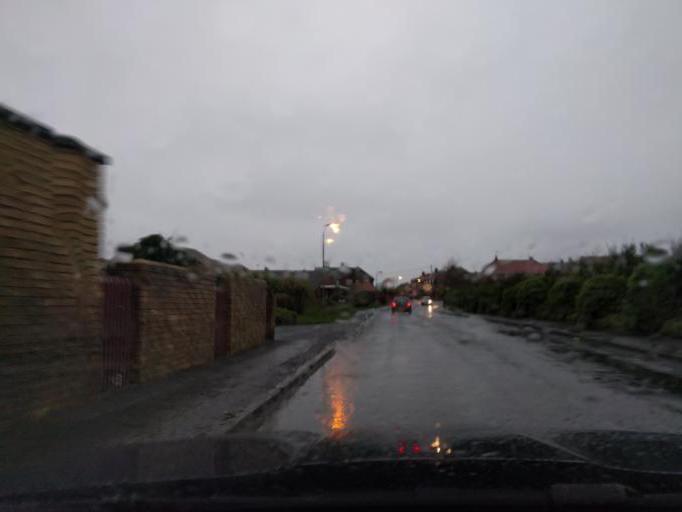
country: GB
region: England
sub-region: Northumberland
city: Newbiggin-by-the-Sea
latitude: 55.1879
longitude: -1.5120
